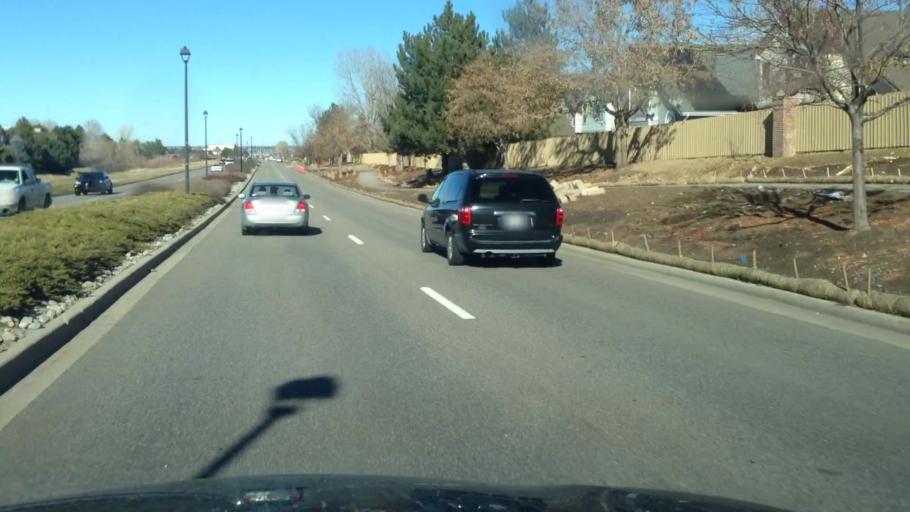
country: US
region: Colorado
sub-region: Douglas County
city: Stonegate
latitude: 39.5252
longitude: -104.7934
